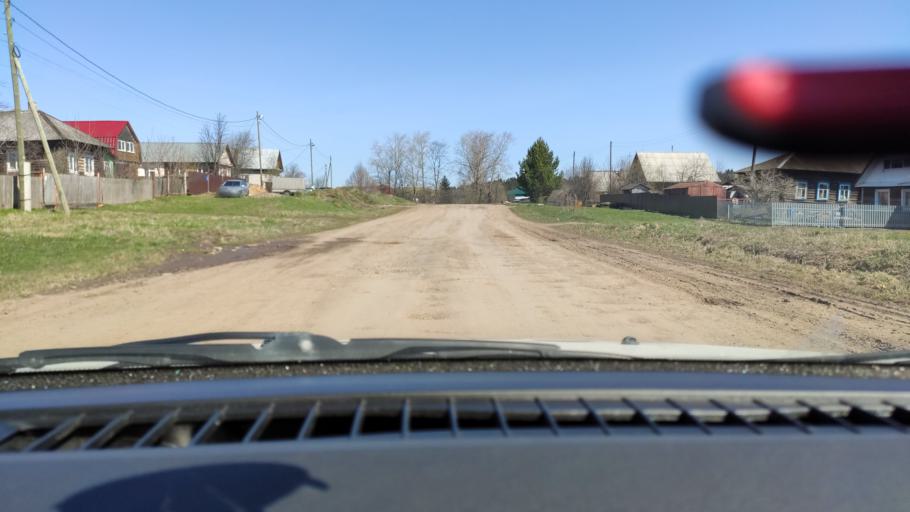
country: RU
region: Perm
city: Bershet'
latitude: 57.7298
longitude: 56.3788
